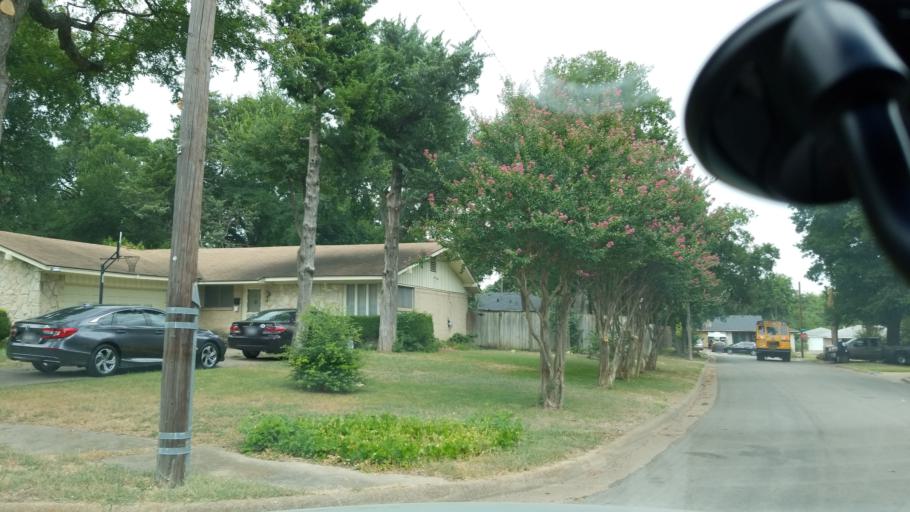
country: US
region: Texas
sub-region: Dallas County
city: Cockrell Hill
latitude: 32.6897
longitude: -96.8492
